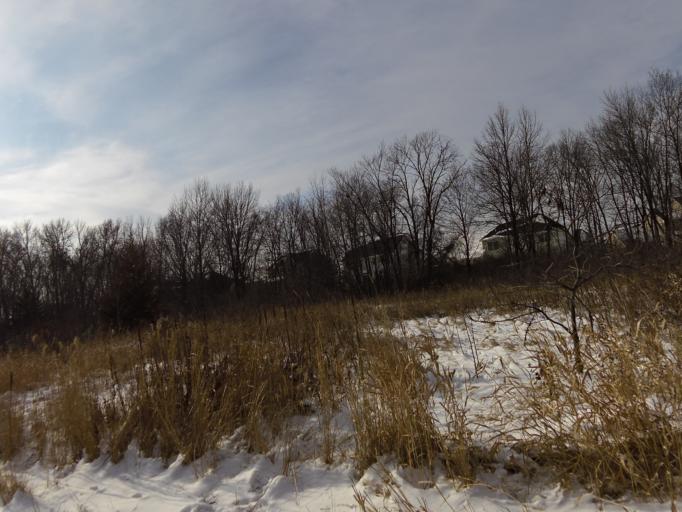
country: US
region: Minnesota
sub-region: Scott County
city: Prior Lake
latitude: 44.7105
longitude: -93.4744
